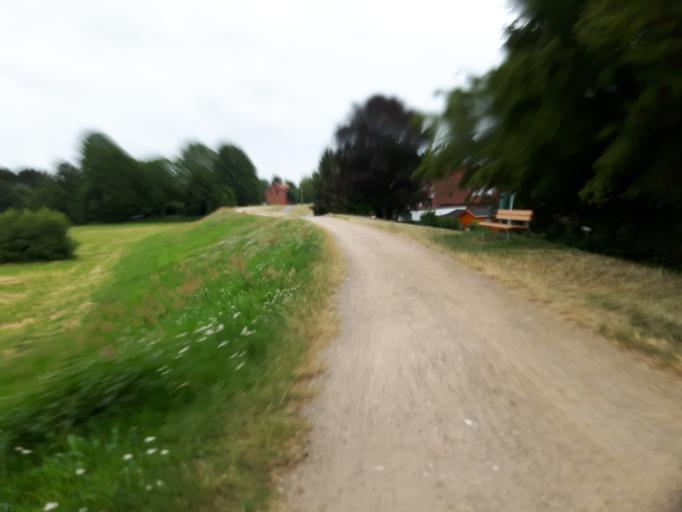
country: DE
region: Lower Saxony
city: Winsen
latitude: 53.3695
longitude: 10.2017
